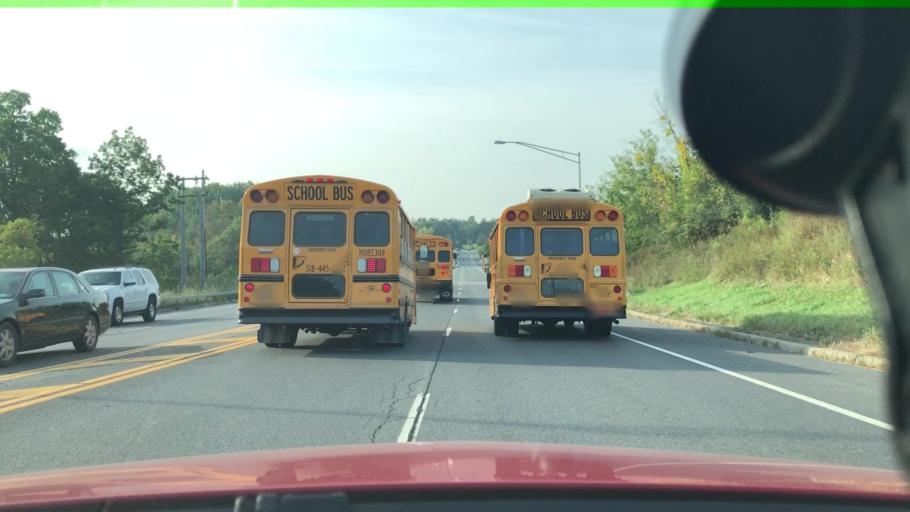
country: US
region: New York
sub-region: Albany County
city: Albany
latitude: 42.6269
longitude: -73.7769
